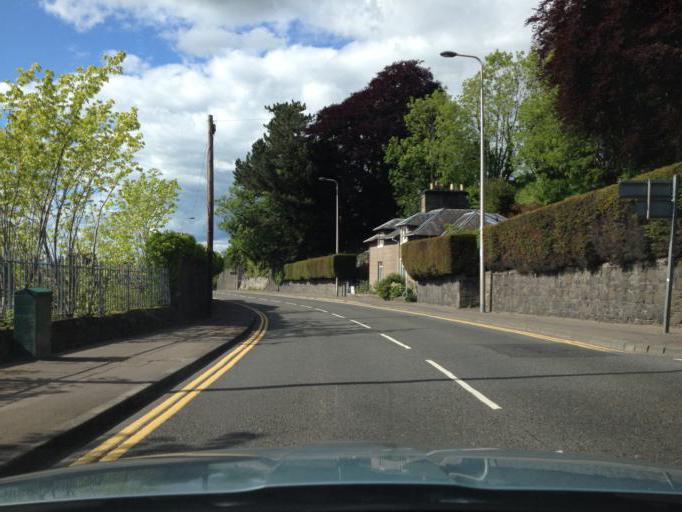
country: GB
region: Scotland
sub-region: Perth and Kinross
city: Perth
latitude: 56.3914
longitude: -3.4191
